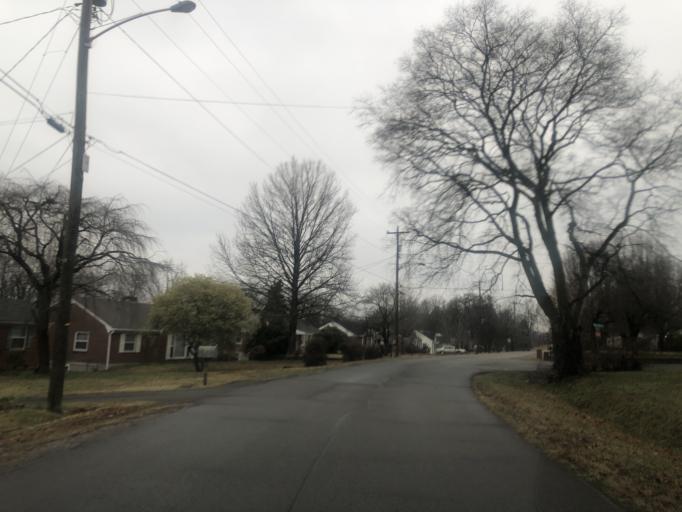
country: US
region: Tennessee
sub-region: Davidson County
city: Lakewood
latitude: 36.1651
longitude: -86.6863
